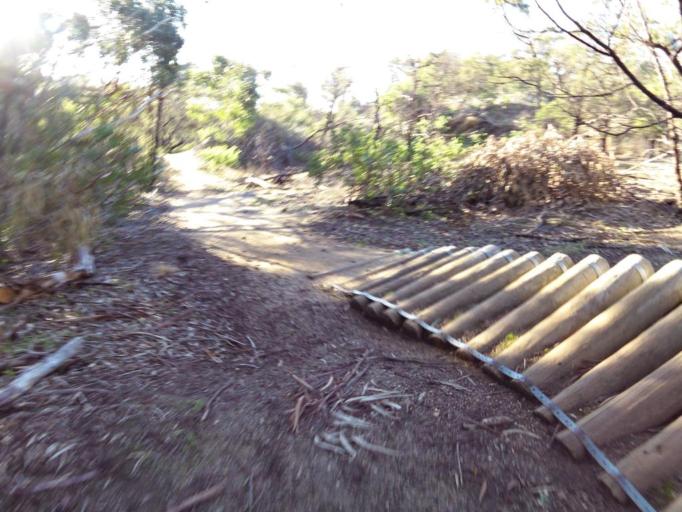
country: AU
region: Victoria
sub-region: Wyndham
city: Little River
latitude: -37.9269
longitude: 144.4428
